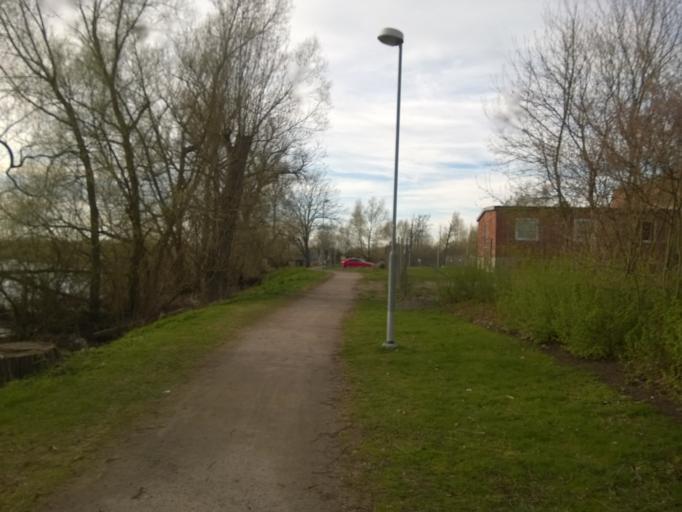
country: SE
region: Skane
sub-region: Kristianstads Kommun
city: Kristianstad
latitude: 56.0315
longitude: 14.1480
